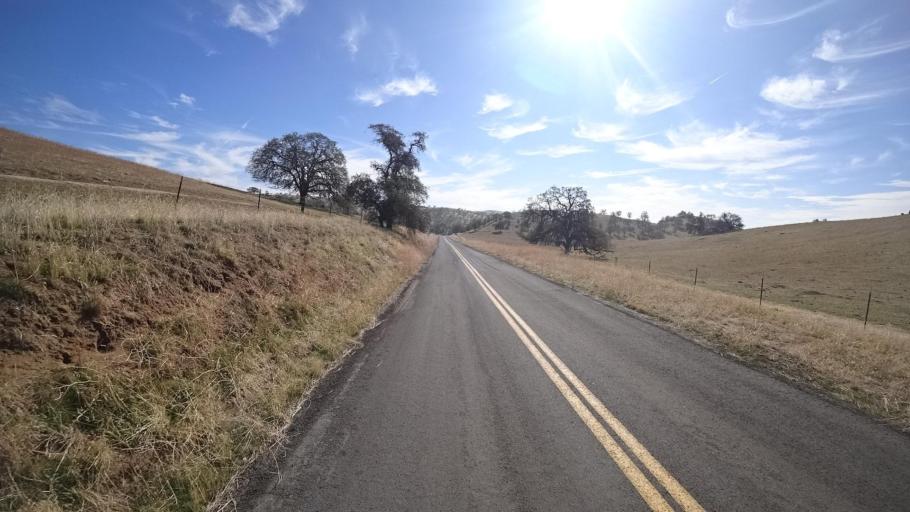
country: US
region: California
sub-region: Kern County
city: Oildale
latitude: 35.6437
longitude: -118.8388
